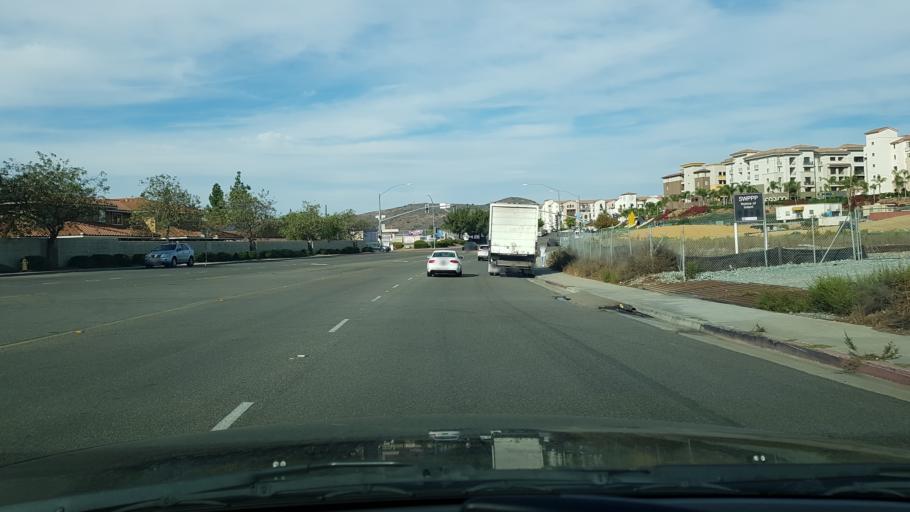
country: US
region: California
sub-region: San Diego County
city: Poway
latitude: 32.9188
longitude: -117.1205
